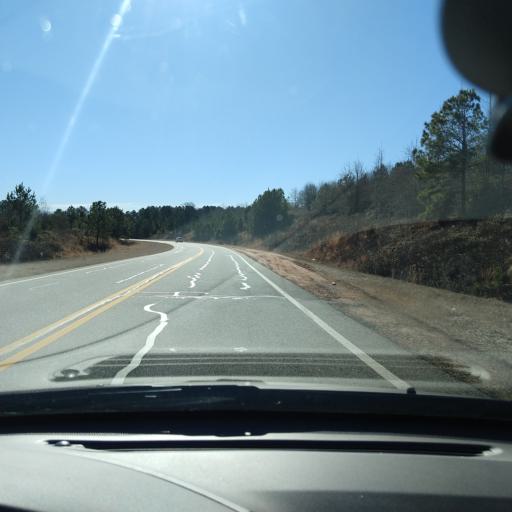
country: US
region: Georgia
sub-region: Walton County
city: Social Circle
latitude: 33.6776
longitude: -83.7035
